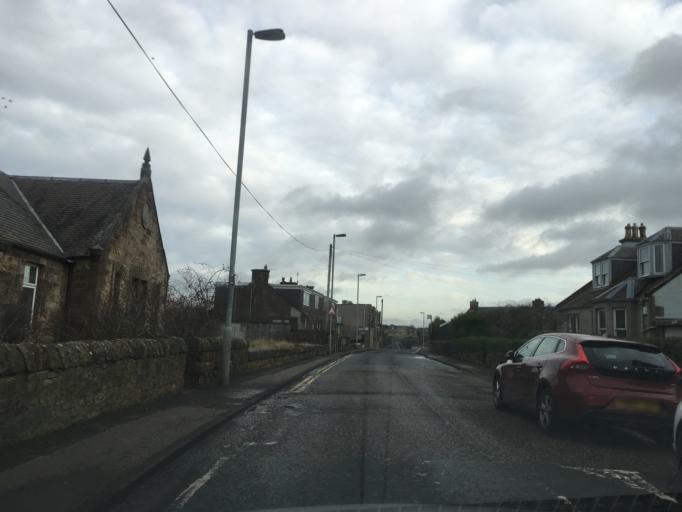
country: GB
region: Scotland
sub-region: Midlothian
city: Penicuik
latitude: 55.8290
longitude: -3.2160
